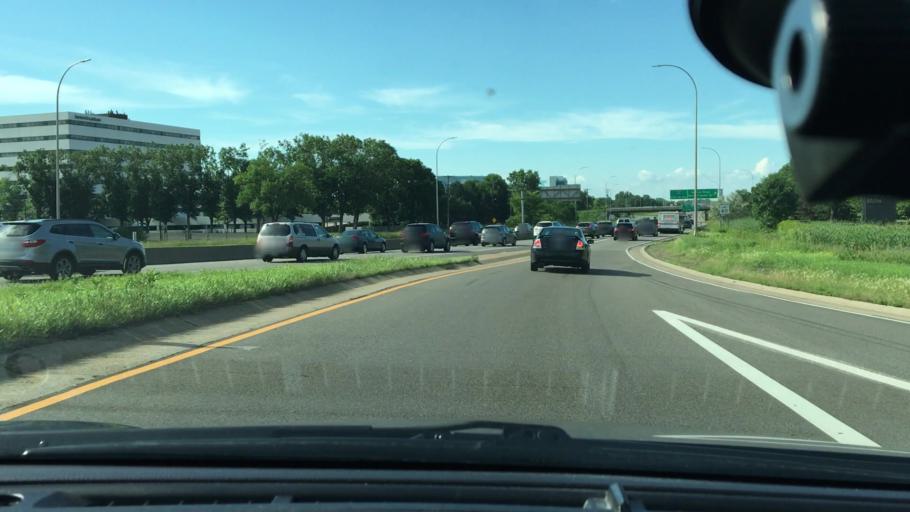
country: US
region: Minnesota
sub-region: Hennepin County
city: Minnetonka Mills
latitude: 44.9757
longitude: -93.4002
